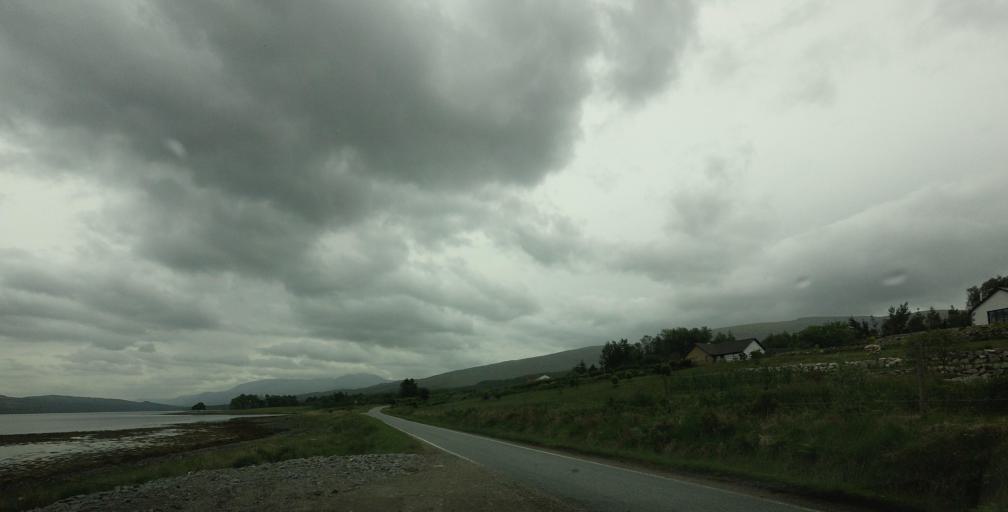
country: GB
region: Scotland
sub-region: Highland
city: Fort William
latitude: 56.8450
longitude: -5.2731
